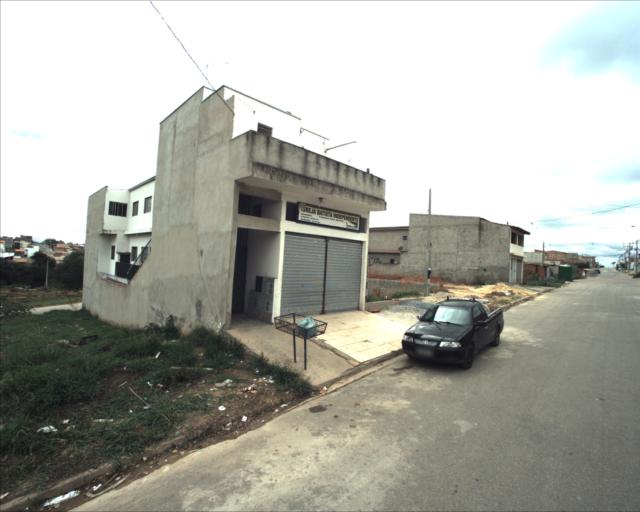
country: BR
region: Sao Paulo
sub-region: Sorocaba
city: Sorocaba
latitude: -23.4375
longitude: -47.5015
